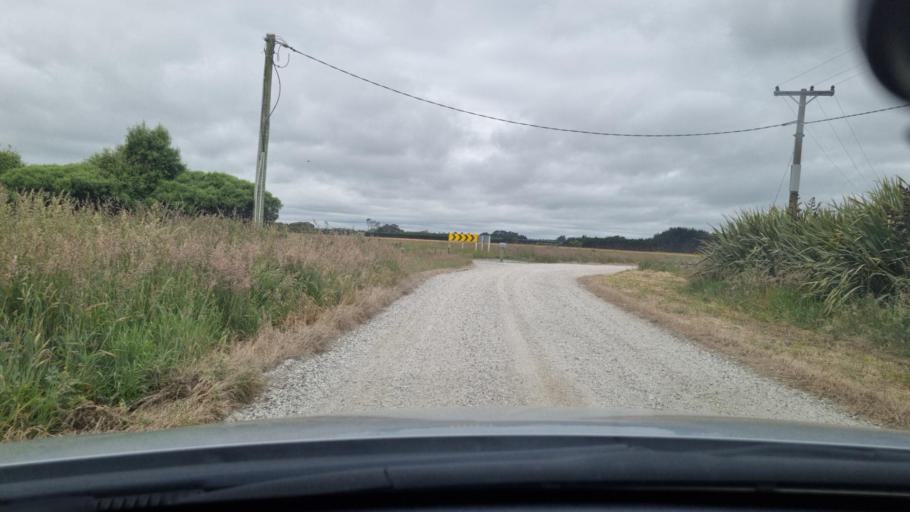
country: NZ
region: Southland
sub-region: Invercargill City
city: Invercargill
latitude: -46.3790
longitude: 168.2881
